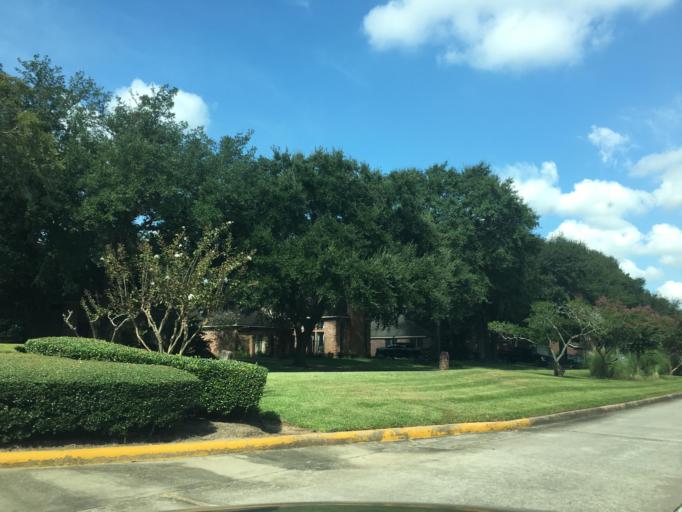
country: US
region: Texas
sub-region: Harris County
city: Spring
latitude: 30.0502
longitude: -95.4447
